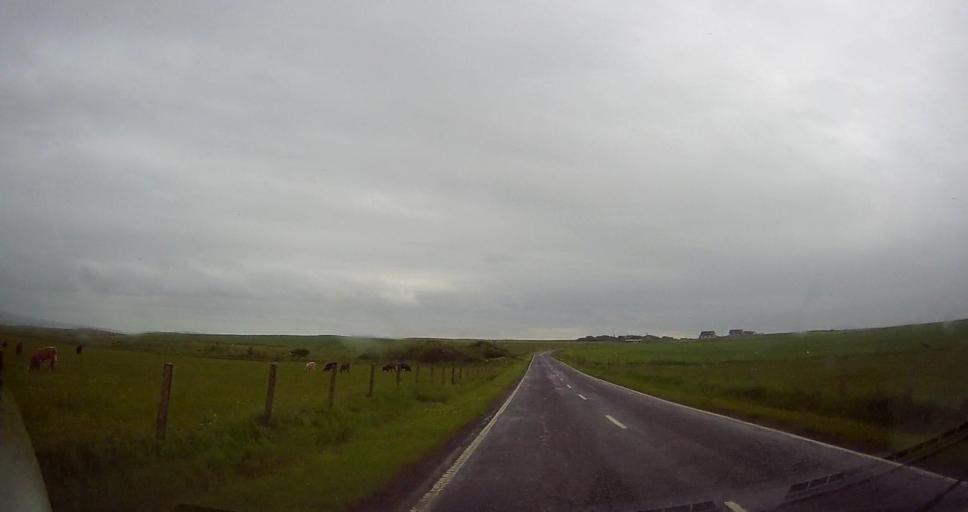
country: GB
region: Scotland
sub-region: Orkney Islands
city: Stromness
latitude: 59.0581
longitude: -3.2823
